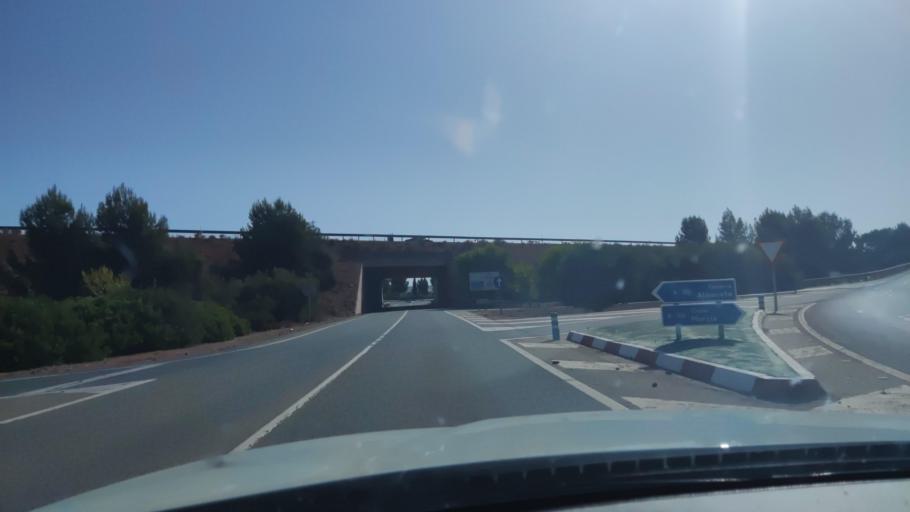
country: ES
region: Castille-La Mancha
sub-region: Provincia de Albacete
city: Hellin
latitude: 38.4944
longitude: -1.6411
